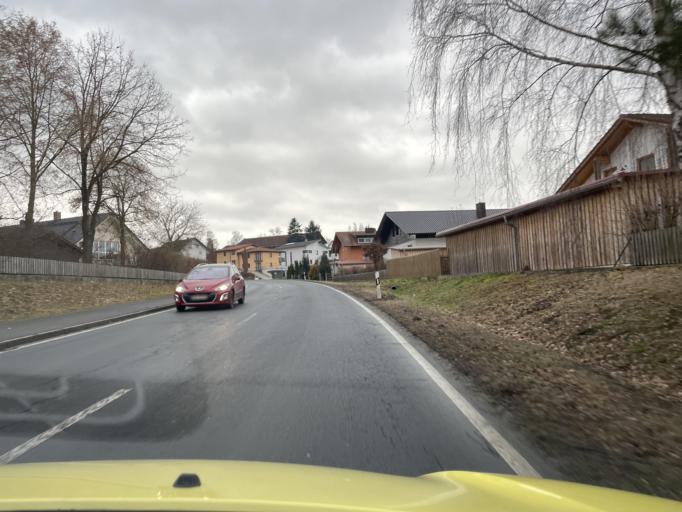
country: DE
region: Bavaria
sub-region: Upper Palatinate
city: Traitsching
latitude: 49.1792
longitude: 12.6761
